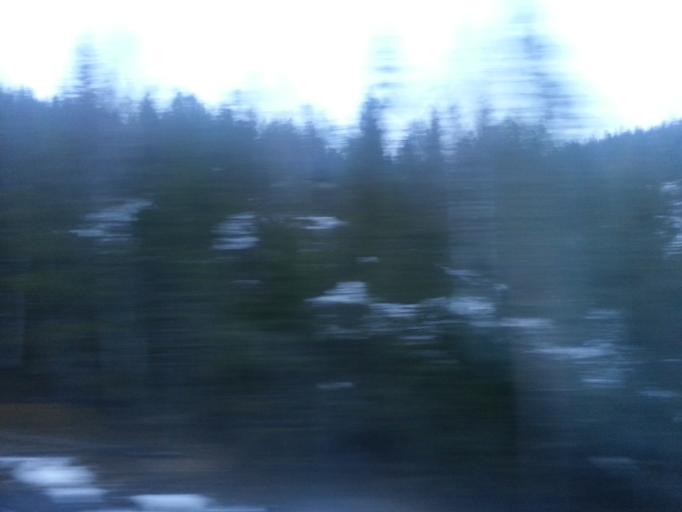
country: NO
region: Sor-Trondelag
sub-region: Rennebu
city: Berkak
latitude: 62.7914
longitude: 10.0152
